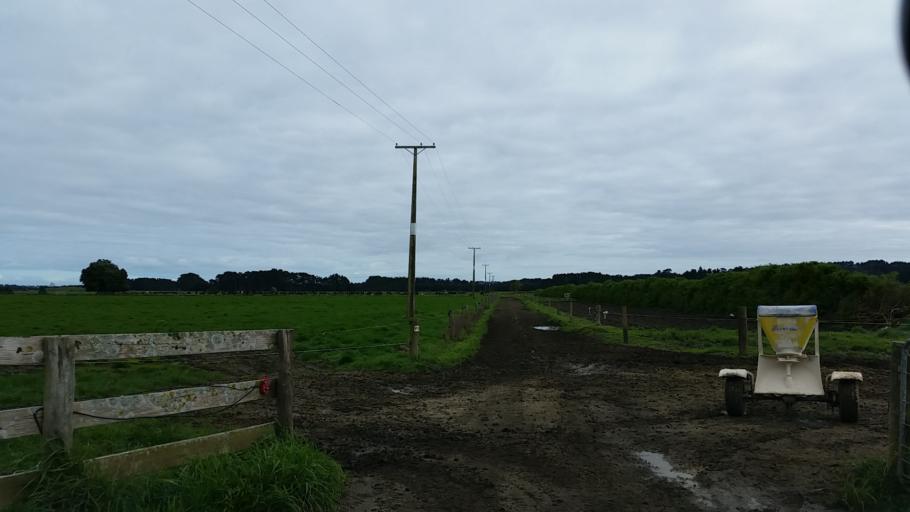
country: NZ
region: Taranaki
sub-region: South Taranaki District
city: Patea
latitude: -39.7251
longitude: 174.6419
